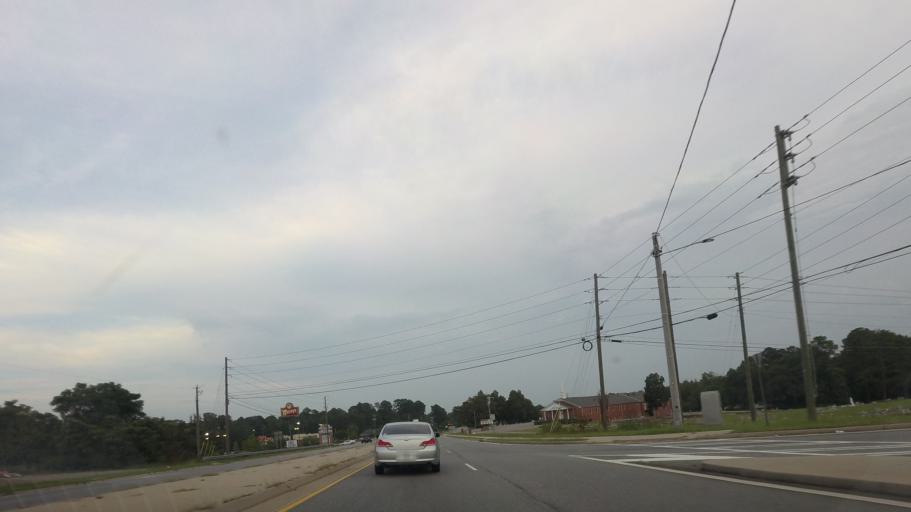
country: US
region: Georgia
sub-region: Peach County
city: Byron
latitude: 32.7439
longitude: -83.7165
